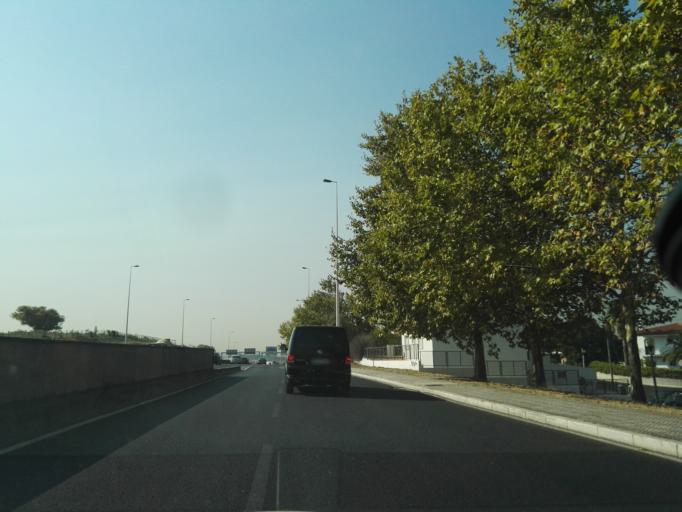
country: PT
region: Lisbon
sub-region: Loures
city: Moscavide
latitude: 38.7619
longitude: -9.1229
